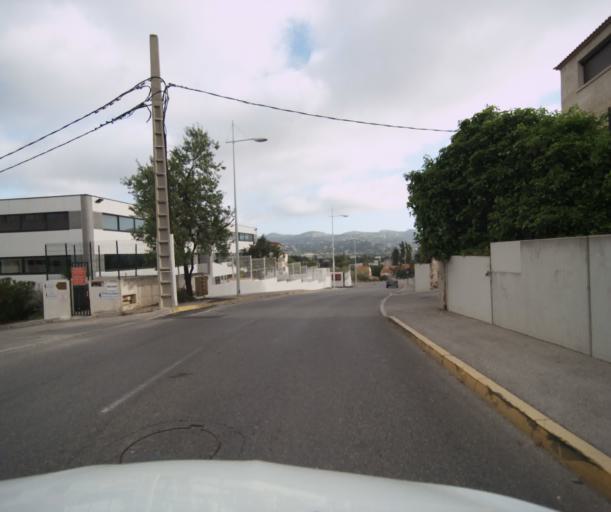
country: FR
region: Provence-Alpes-Cote d'Azur
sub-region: Departement du Var
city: Six-Fours-les-Plages
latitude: 43.1088
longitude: 5.8430
